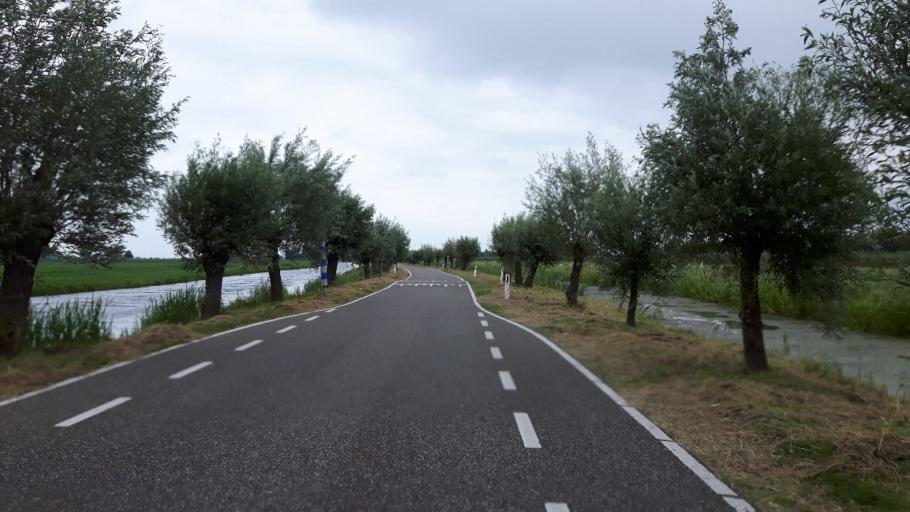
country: NL
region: South Holland
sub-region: Gemeente Nieuwkoop
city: Nieuwkoop
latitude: 52.1226
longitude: 4.7553
